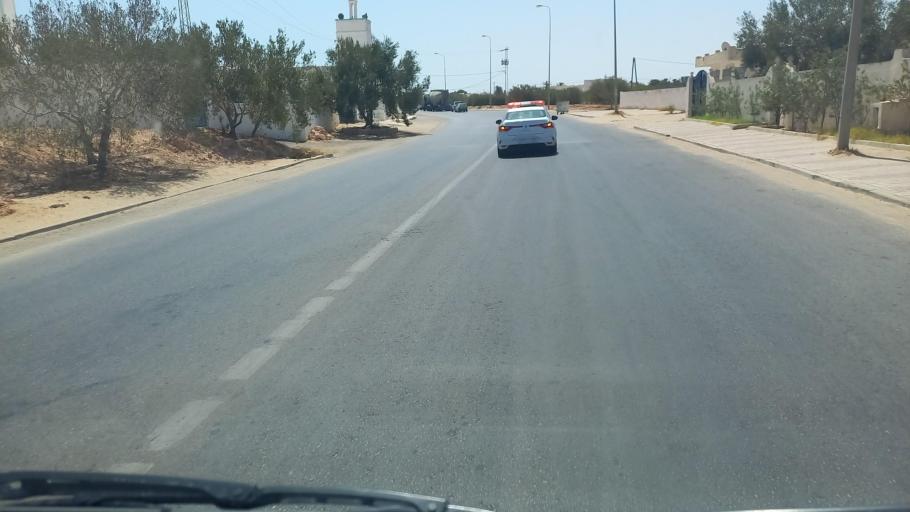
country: TN
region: Madanin
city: Houmt Souk
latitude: 33.7820
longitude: 10.8889
